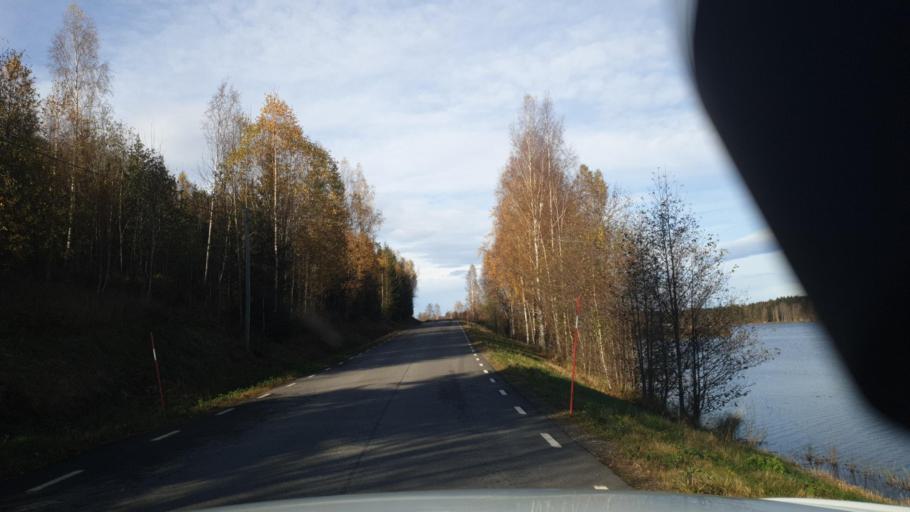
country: SE
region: Vaermland
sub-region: Eda Kommun
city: Charlottenberg
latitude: 59.9436
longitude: 12.5221
